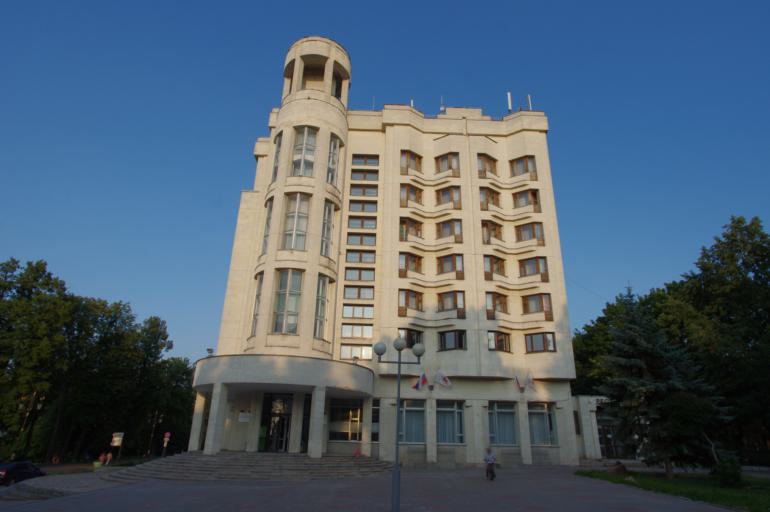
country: RU
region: Nizjnij Novgorod
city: Nizhniy Novgorod
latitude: 56.3286
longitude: 44.0192
